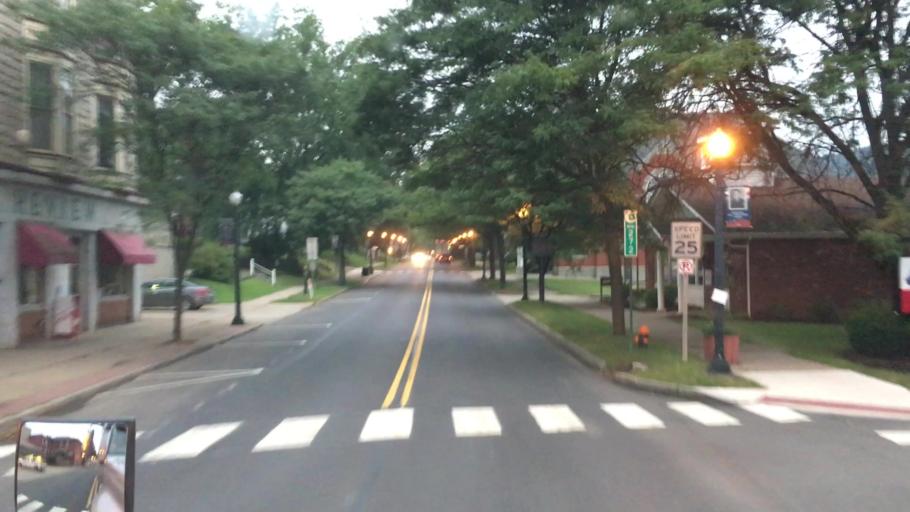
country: US
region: Pennsylvania
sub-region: Bradford County
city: Towanda
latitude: 41.7683
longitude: -76.4431
